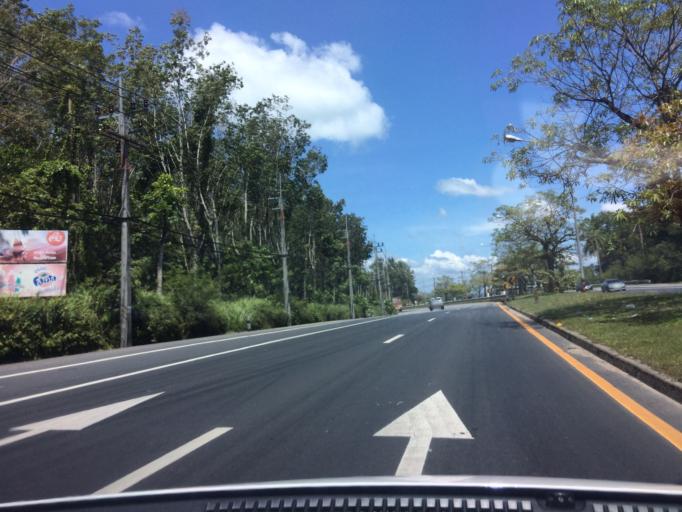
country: TH
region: Phuket
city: Thalang
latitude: 8.1418
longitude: 98.3415
